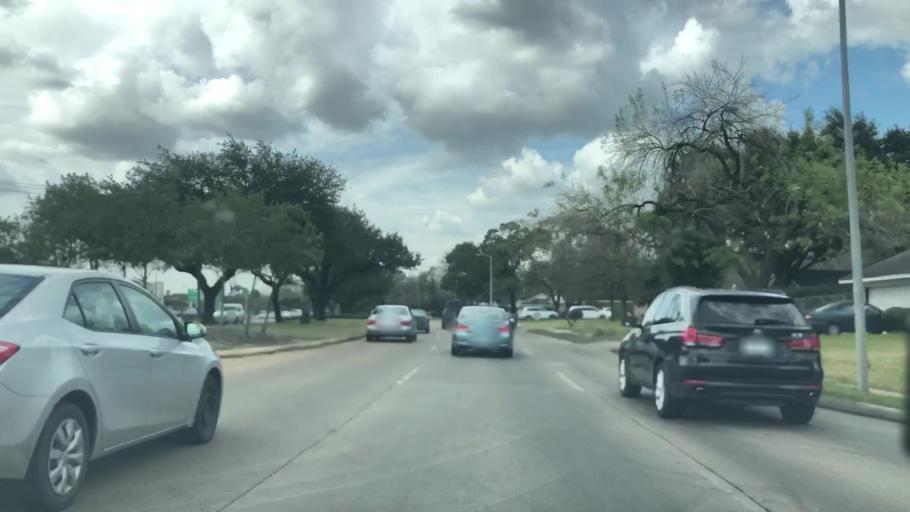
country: US
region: Texas
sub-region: Harris County
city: Bellaire
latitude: 29.6905
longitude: -95.5036
